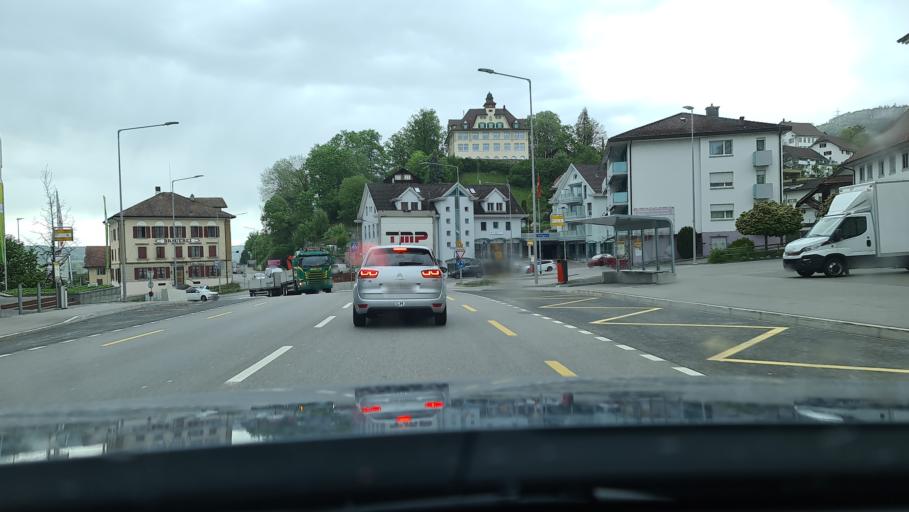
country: CH
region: Lucerne
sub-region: Sursee District
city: Bueron
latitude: 47.2131
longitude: 8.0951
